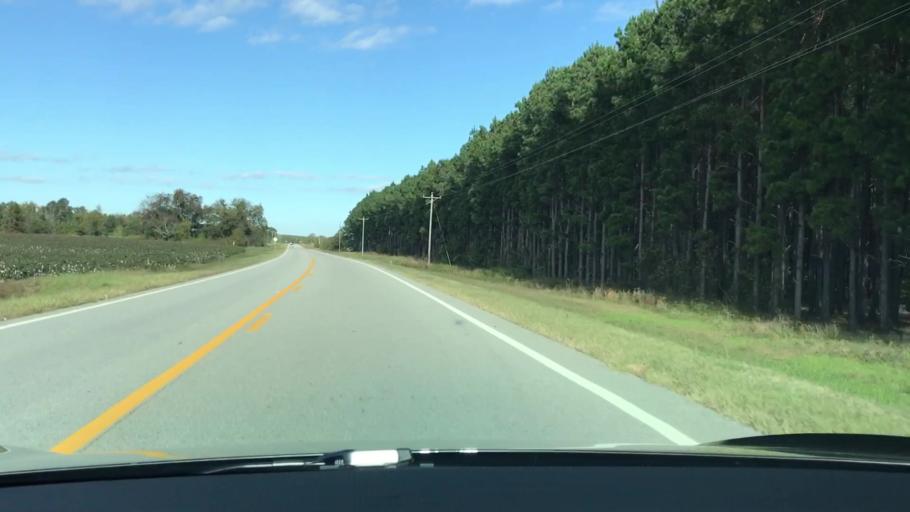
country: US
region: Georgia
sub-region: Glascock County
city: Gibson
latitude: 33.2856
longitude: -82.5064
